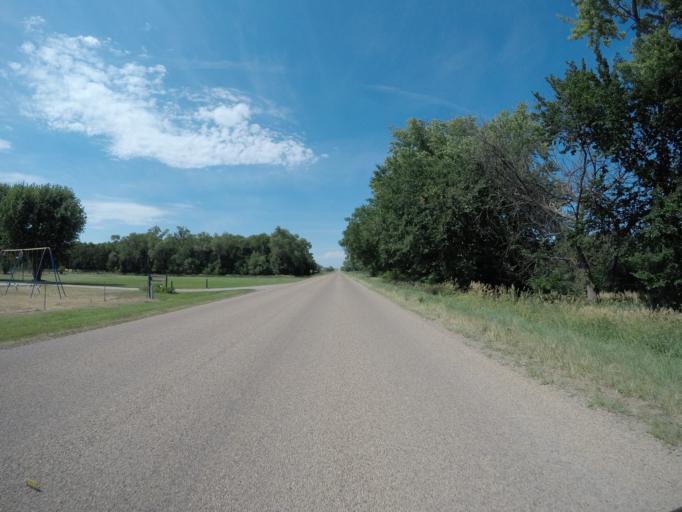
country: US
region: Nebraska
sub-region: Webster County
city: Red Cloud
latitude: 40.0772
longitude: -98.3303
